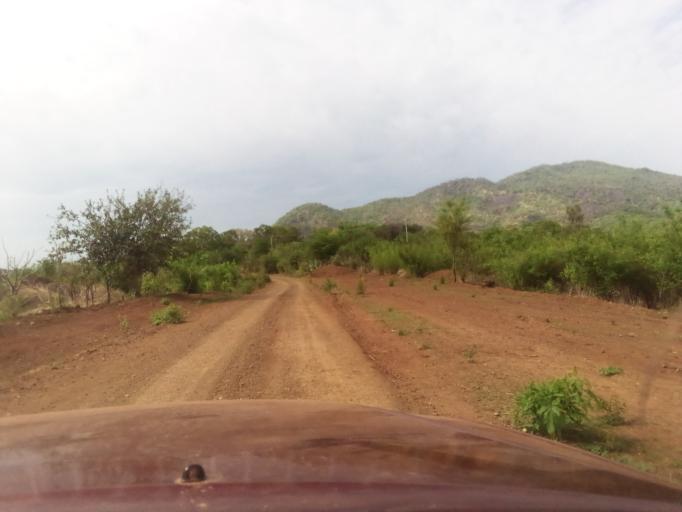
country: ET
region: Oromiya
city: Mendi
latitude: 10.0424
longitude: 35.3062
